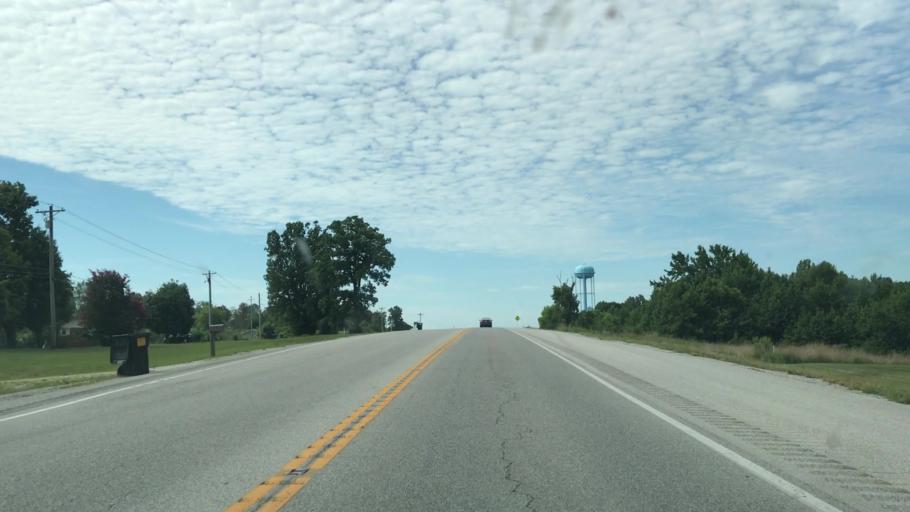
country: US
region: Kentucky
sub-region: Edmonson County
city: Brownsville
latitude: 37.1066
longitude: -86.2294
